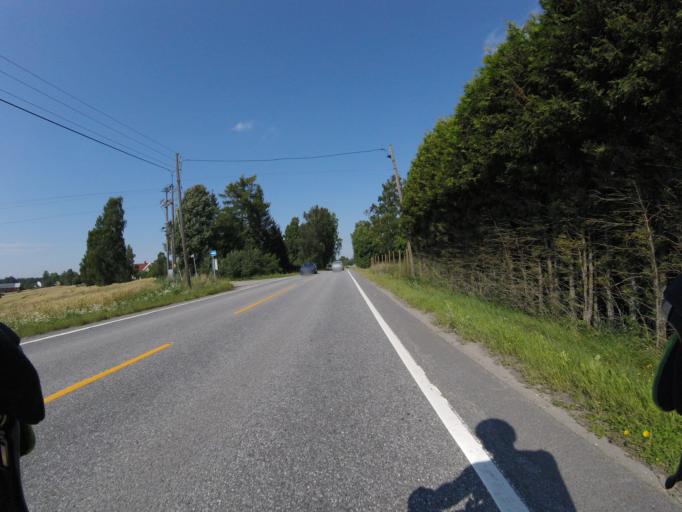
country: NO
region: Akershus
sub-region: Sorum
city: Frogner
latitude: 60.0465
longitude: 11.1184
